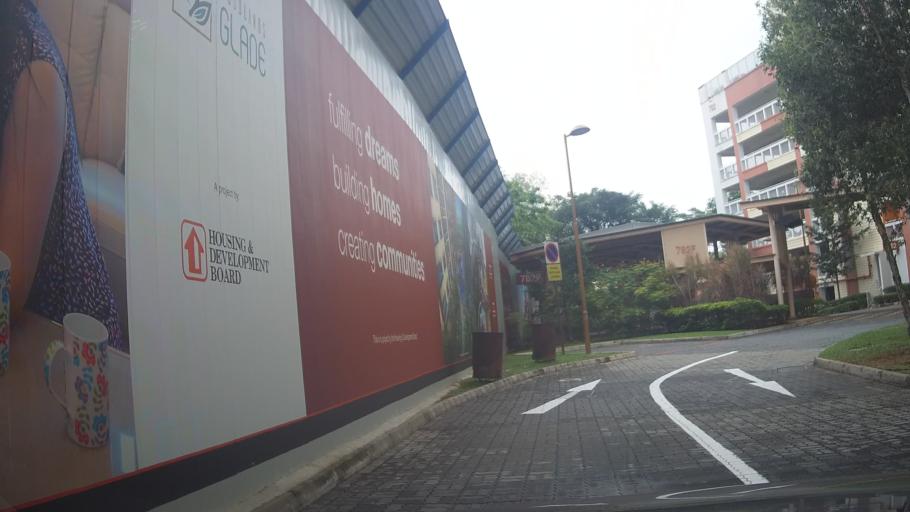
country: MY
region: Johor
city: Johor Bahru
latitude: 1.4482
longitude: 103.8028
